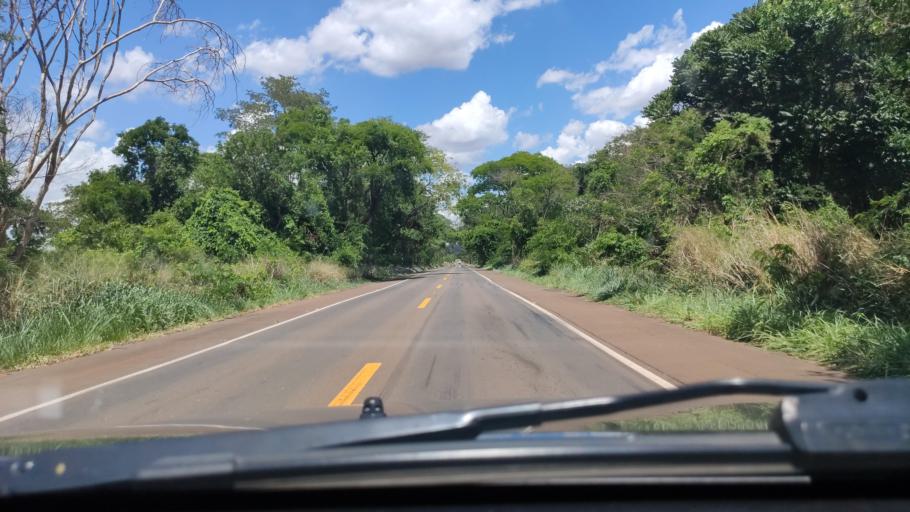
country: BR
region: Sao Paulo
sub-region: Boa Esperanca Do Sul
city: Boa Esperanca do Sul
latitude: -22.0697
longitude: -48.4185
